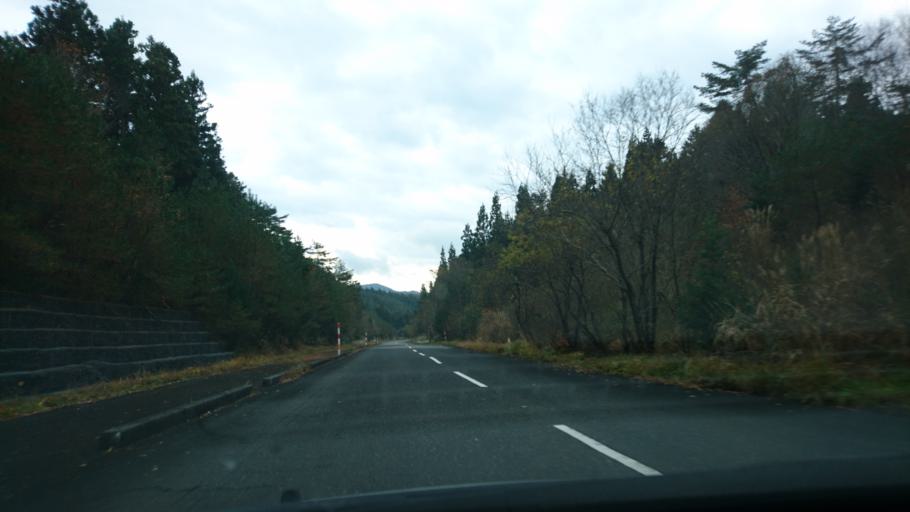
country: JP
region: Iwate
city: Ichinoseki
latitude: 38.9227
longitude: 140.9090
